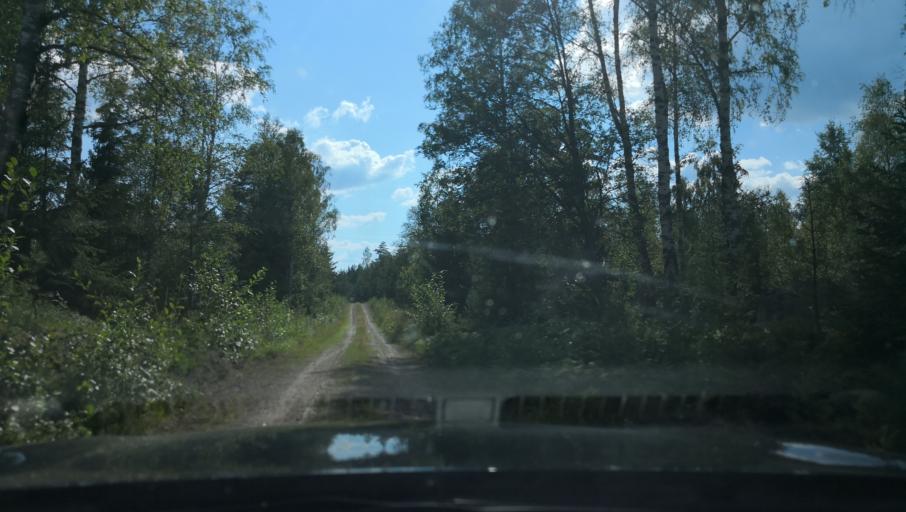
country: SE
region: Vaestmanland
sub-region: Vasteras
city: Skultuna
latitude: 59.7169
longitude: 16.3776
